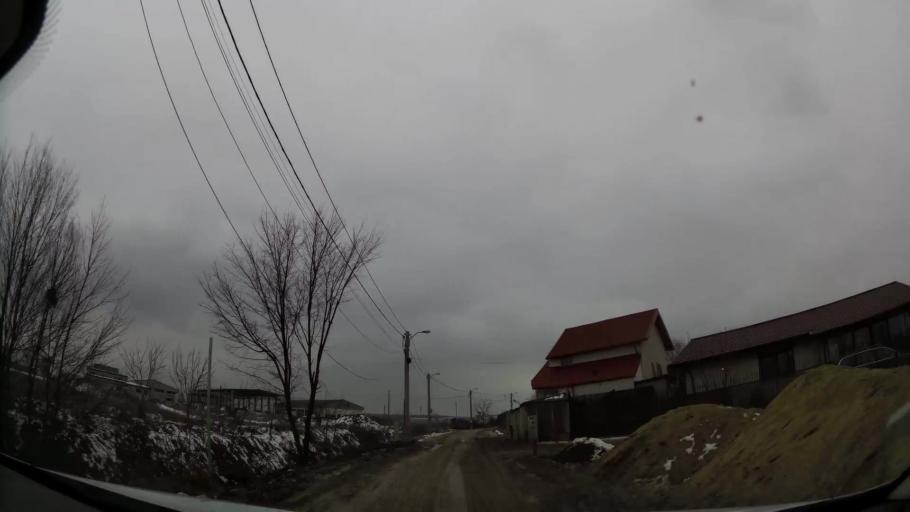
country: RO
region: Ilfov
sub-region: Comuna Otopeni
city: Otopeni
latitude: 44.5475
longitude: 26.0904
